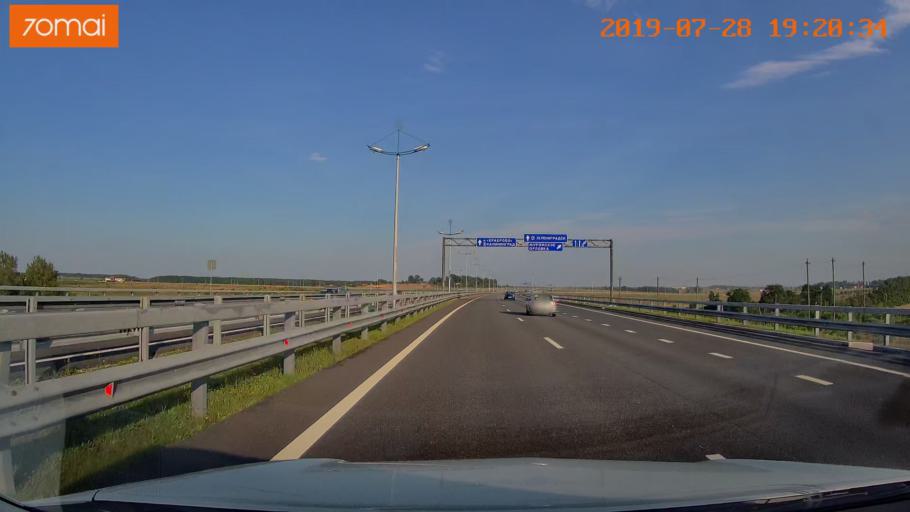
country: RU
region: Kaliningrad
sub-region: Zelenogradskiy Rayon
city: Zelenogradsk
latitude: 54.9140
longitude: 20.4893
